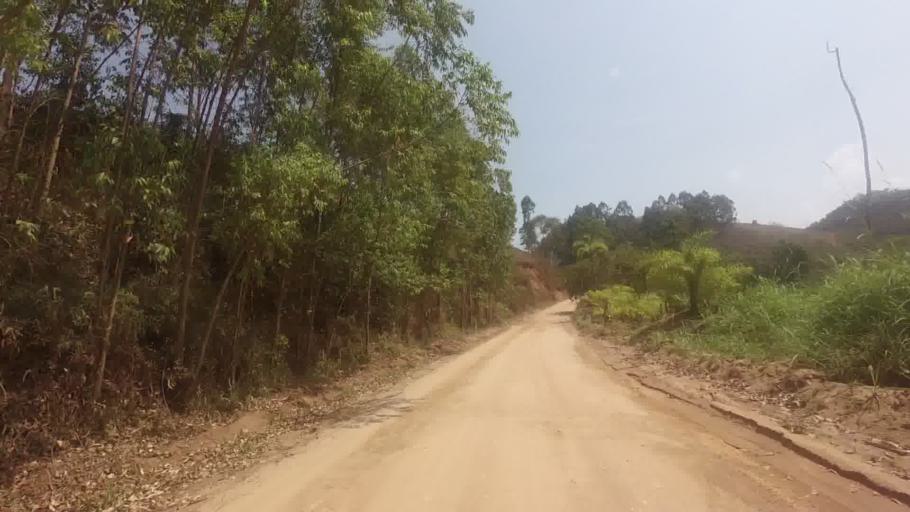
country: BR
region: Espirito Santo
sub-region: Mimoso Do Sul
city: Mimoso do Sul
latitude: -20.9446
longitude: -41.4042
